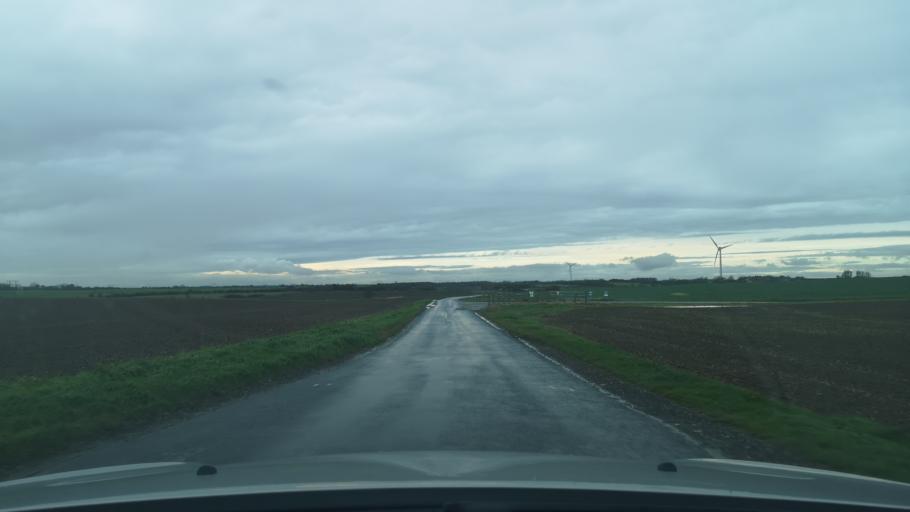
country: GB
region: England
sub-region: East Riding of Yorkshire
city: Easington
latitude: 53.6637
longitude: 0.0985
